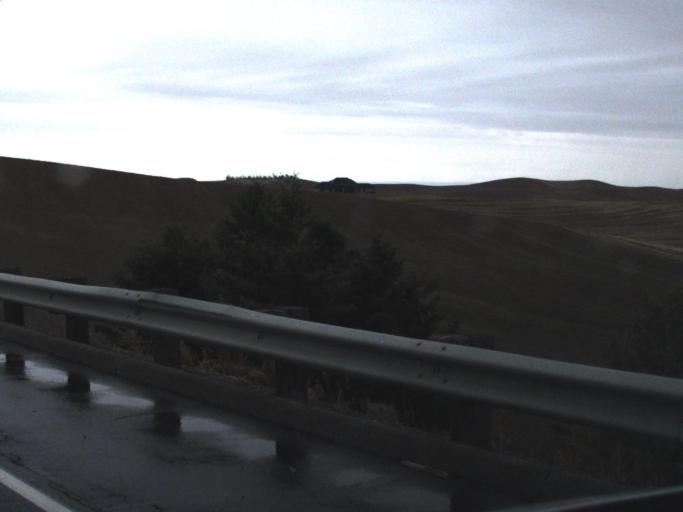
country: US
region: Washington
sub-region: Whitman County
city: Pullman
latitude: 46.7168
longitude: -117.2192
